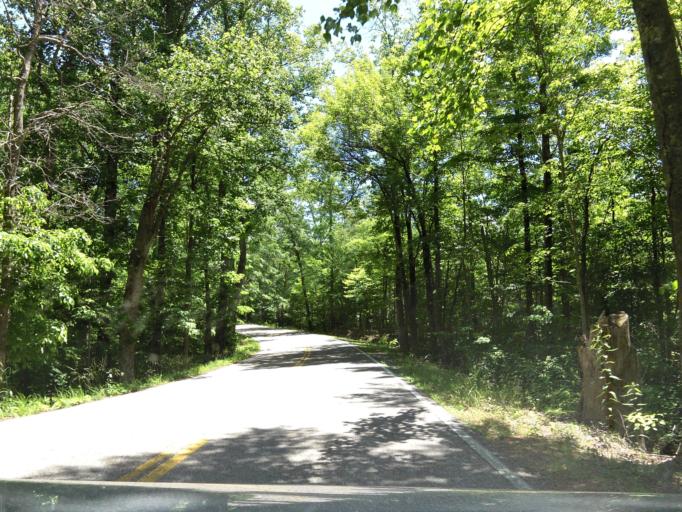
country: US
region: North Carolina
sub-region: Graham County
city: Robbinsville
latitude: 35.5077
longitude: -83.9623
